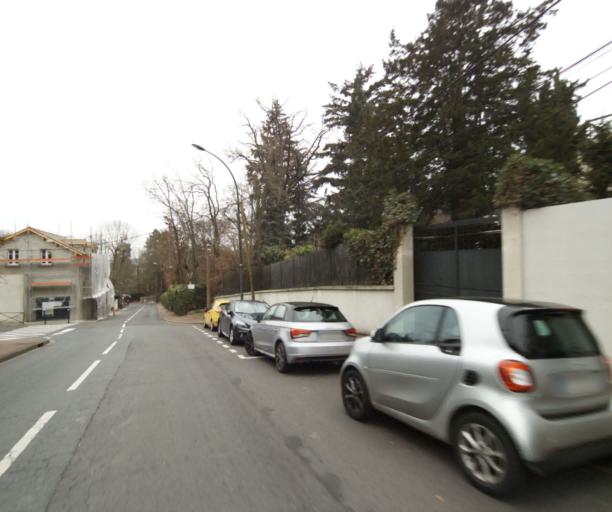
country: FR
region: Ile-de-France
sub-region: Departement des Hauts-de-Seine
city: Garches
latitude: 48.8509
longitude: 2.1910
